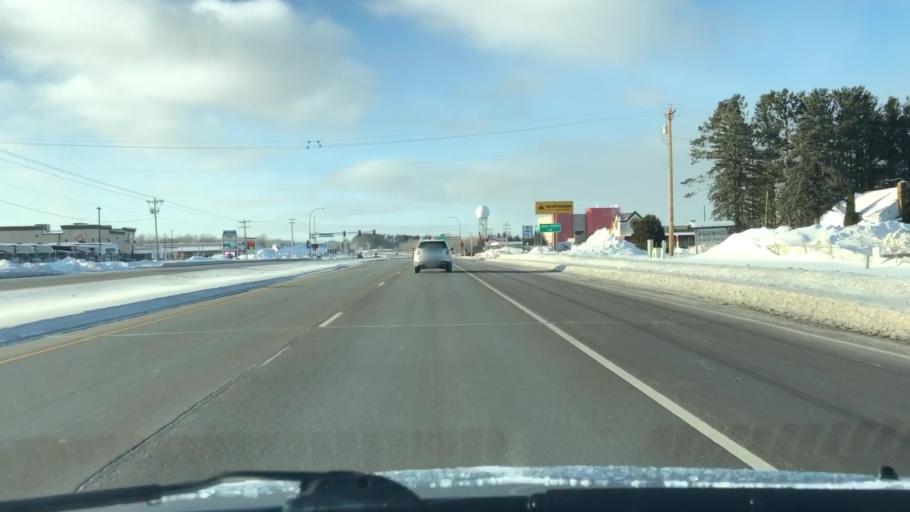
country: US
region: Minnesota
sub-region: Saint Louis County
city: Hermantown
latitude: 46.8323
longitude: -92.2032
